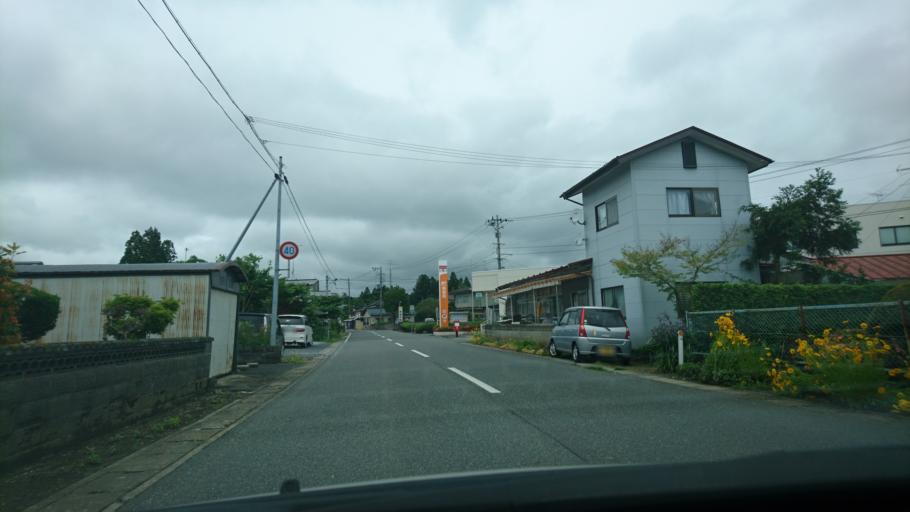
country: JP
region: Iwate
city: Ichinoseki
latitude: 38.9423
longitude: 141.0545
